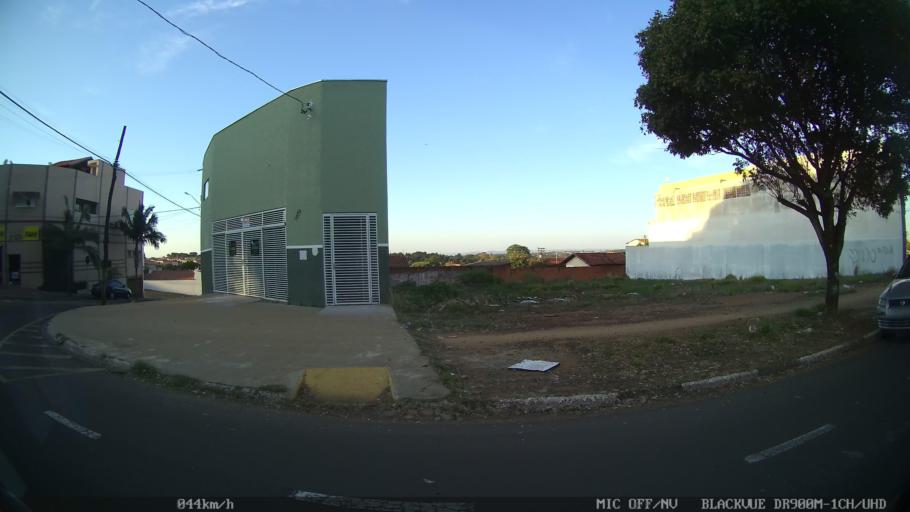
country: BR
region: Sao Paulo
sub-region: Franca
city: Franca
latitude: -20.5044
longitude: -47.3975
